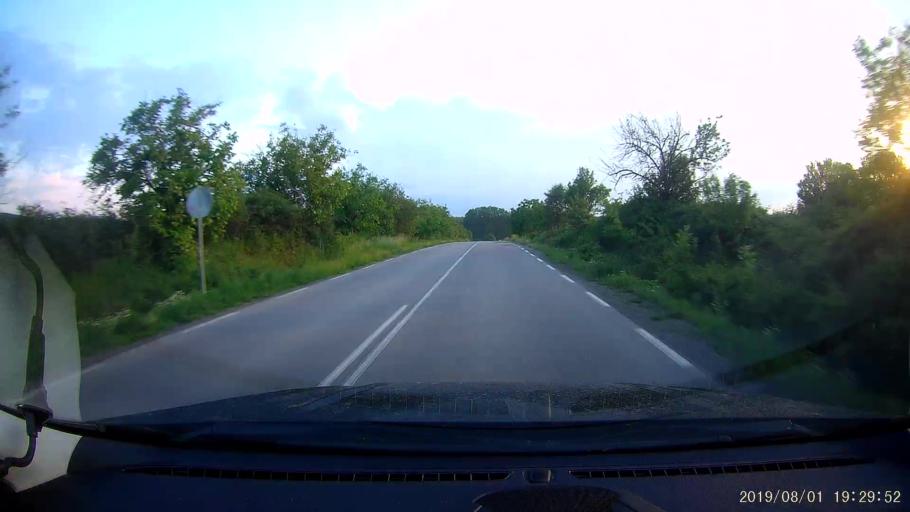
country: BG
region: Burgas
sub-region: Obshtina Sungurlare
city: Sungurlare
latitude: 42.8211
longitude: 26.9000
